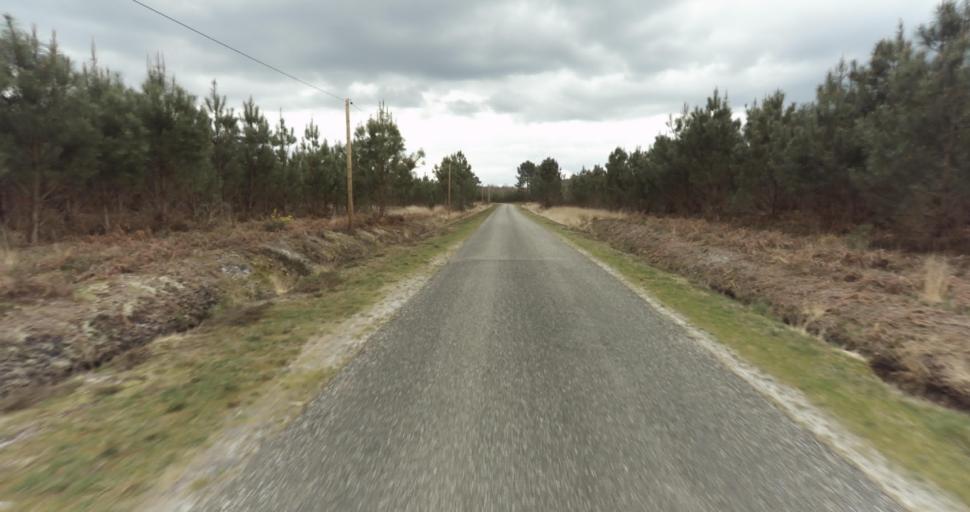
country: FR
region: Aquitaine
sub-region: Departement des Landes
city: Sarbazan
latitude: 44.0079
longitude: -0.3370
